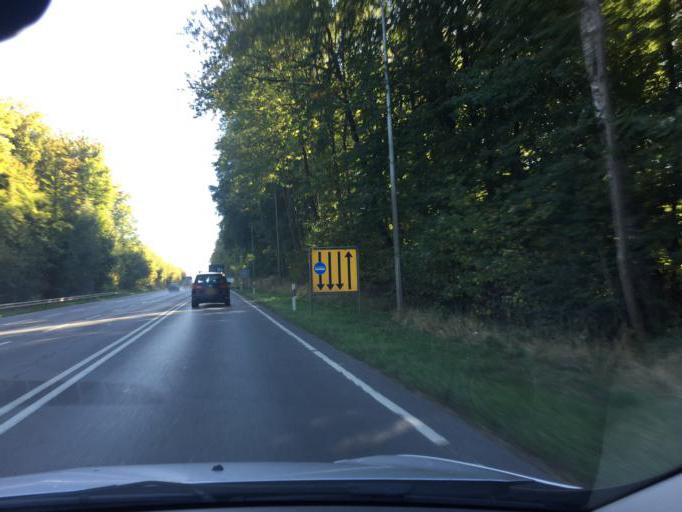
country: LU
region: Luxembourg
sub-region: Canton de Luxembourg
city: Sandweiler
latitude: 49.6146
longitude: 6.1885
